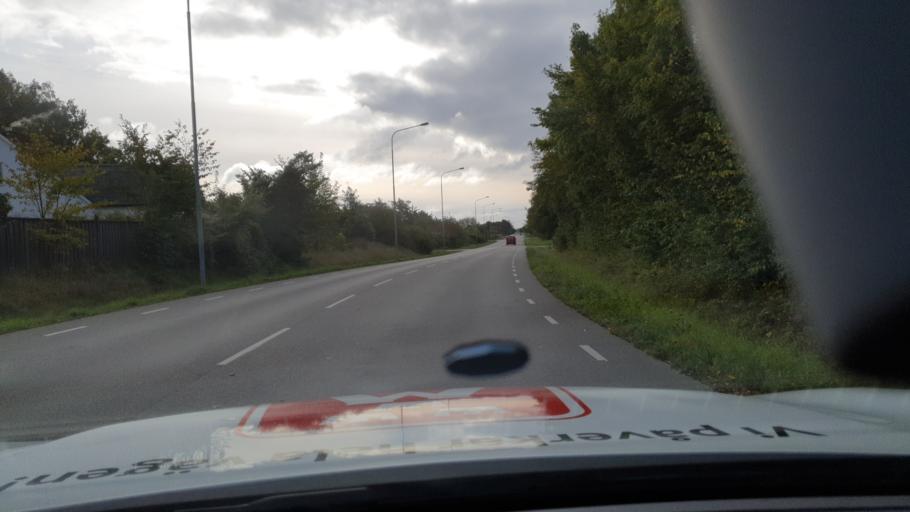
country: SE
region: Skane
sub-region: Vellinge Kommun
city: Vellinge
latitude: 55.4665
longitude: 13.0168
